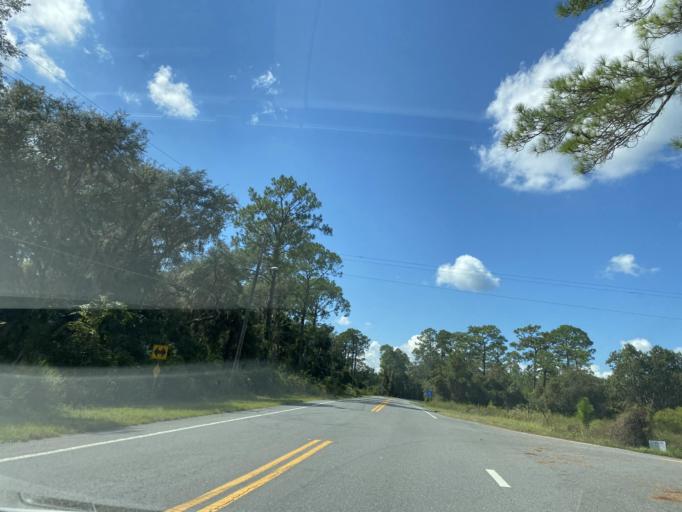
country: US
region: Florida
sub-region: Lake County
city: Lake Mack-Forest Hills
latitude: 29.0147
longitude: -81.4629
